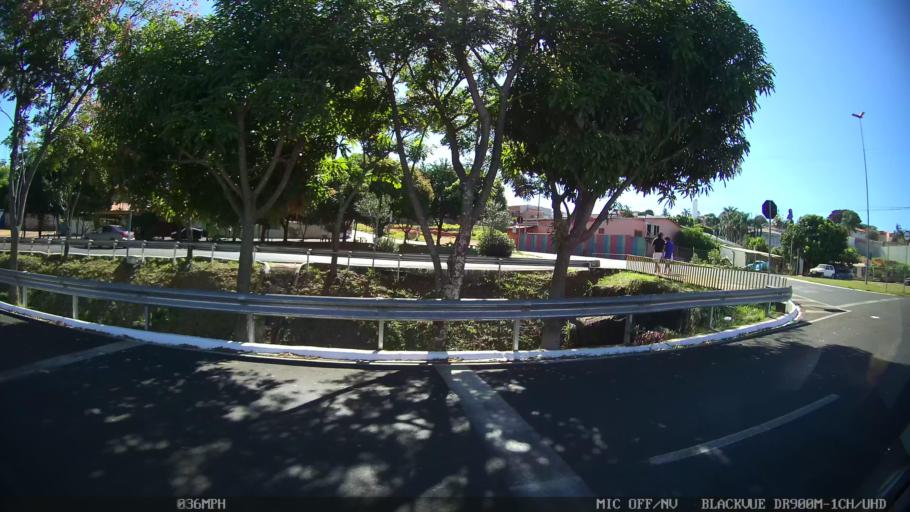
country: BR
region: Sao Paulo
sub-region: Franca
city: Franca
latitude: -20.5211
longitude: -47.3743
